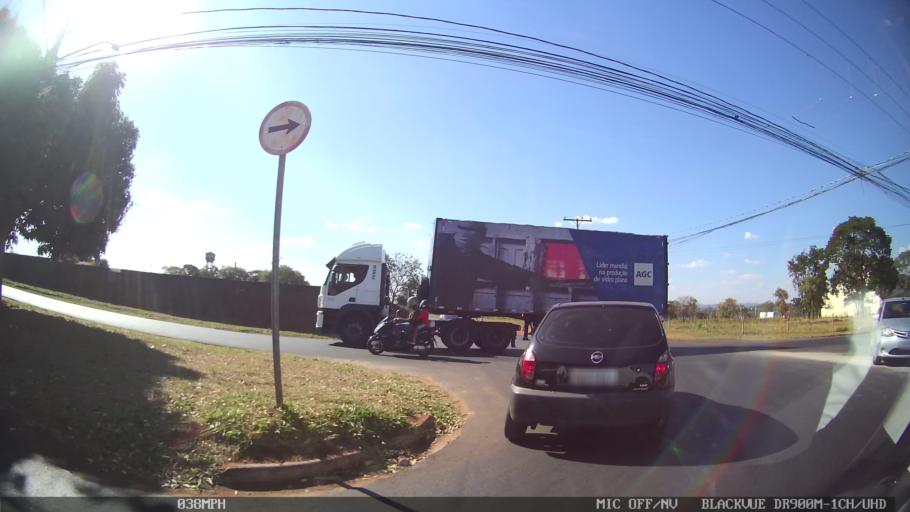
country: BR
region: Sao Paulo
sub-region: Ribeirao Preto
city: Ribeirao Preto
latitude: -21.1519
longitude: -47.7621
